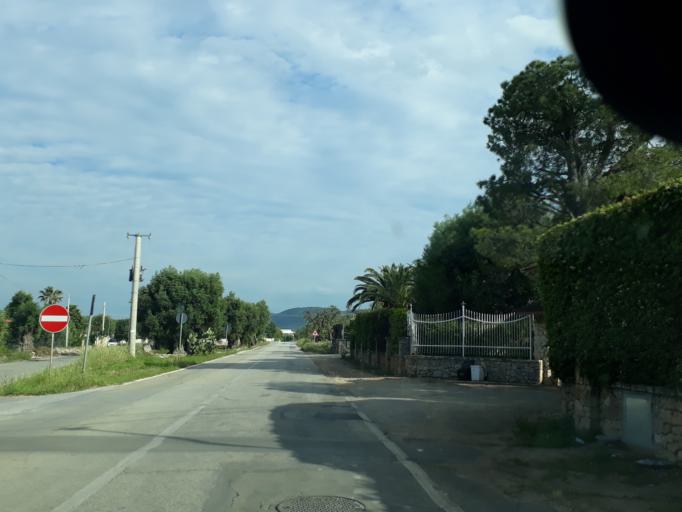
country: IT
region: Apulia
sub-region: Provincia di Brindisi
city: Fasano
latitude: 40.8277
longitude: 17.3681
